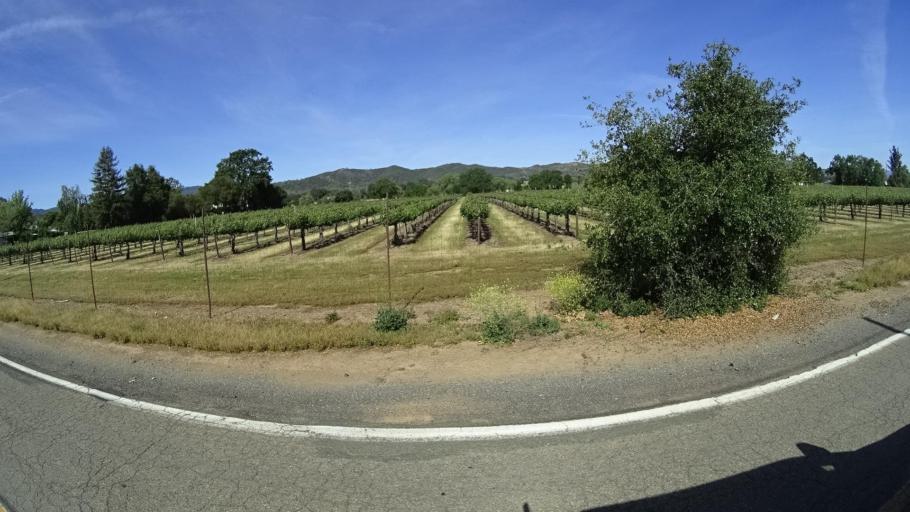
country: US
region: California
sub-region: Lake County
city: Kelseyville
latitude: 38.9596
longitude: -122.8858
